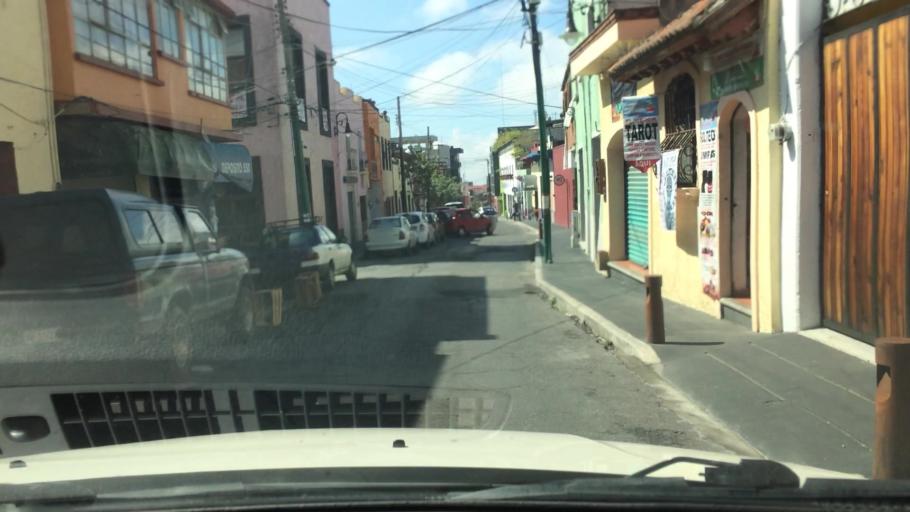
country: MX
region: Morelos
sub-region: Cuernavaca
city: Cuernavaca
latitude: 18.9281
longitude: -99.2381
